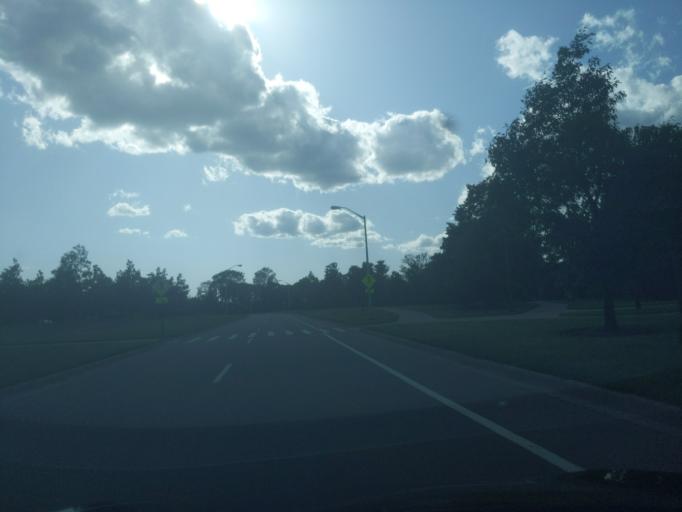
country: US
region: Michigan
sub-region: Ingham County
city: East Lansing
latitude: 42.7200
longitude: -84.4888
